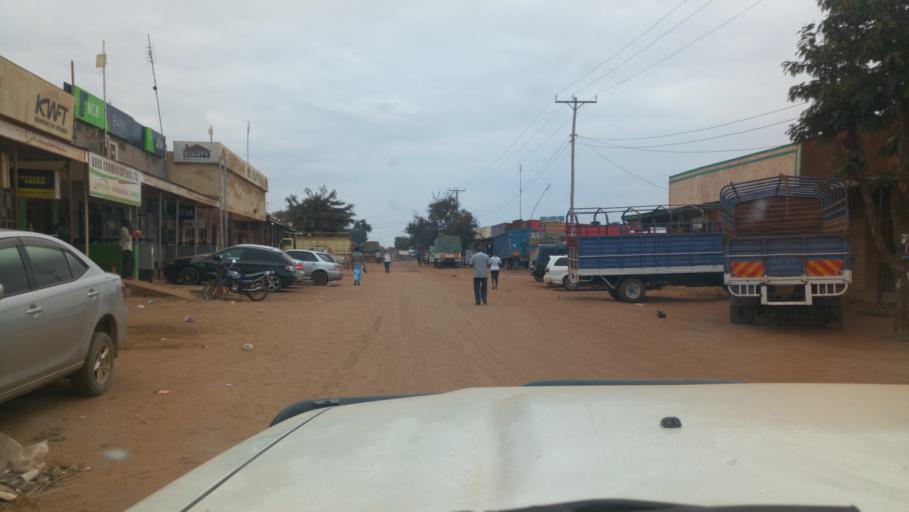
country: KE
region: Kitui
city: Kitui
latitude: -1.8480
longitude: 38.2077
